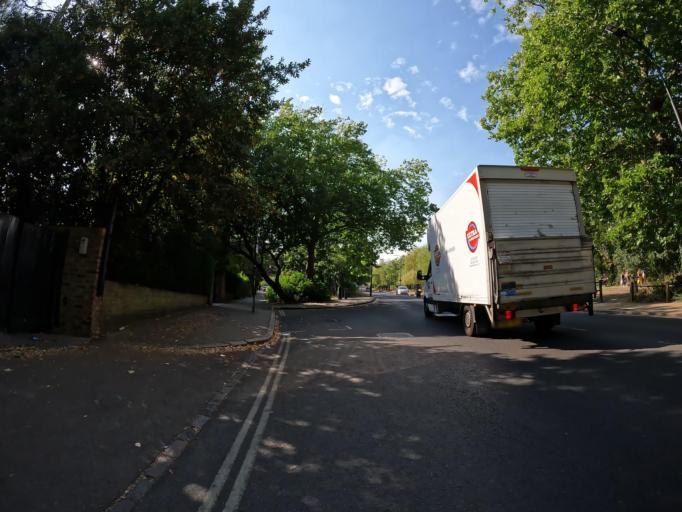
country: GB
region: England
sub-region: Greater London
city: Hadley Wood
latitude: 51.6606
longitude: -0.1735
